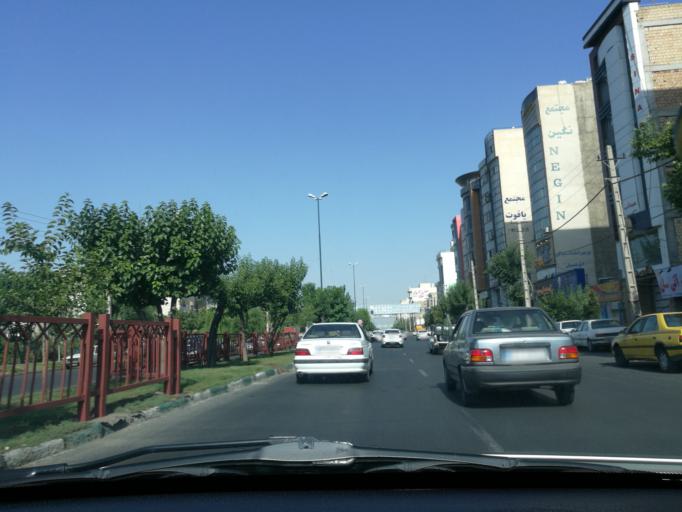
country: IR
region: Alborz
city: Karaj
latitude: 35.8308
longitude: 51.0092
